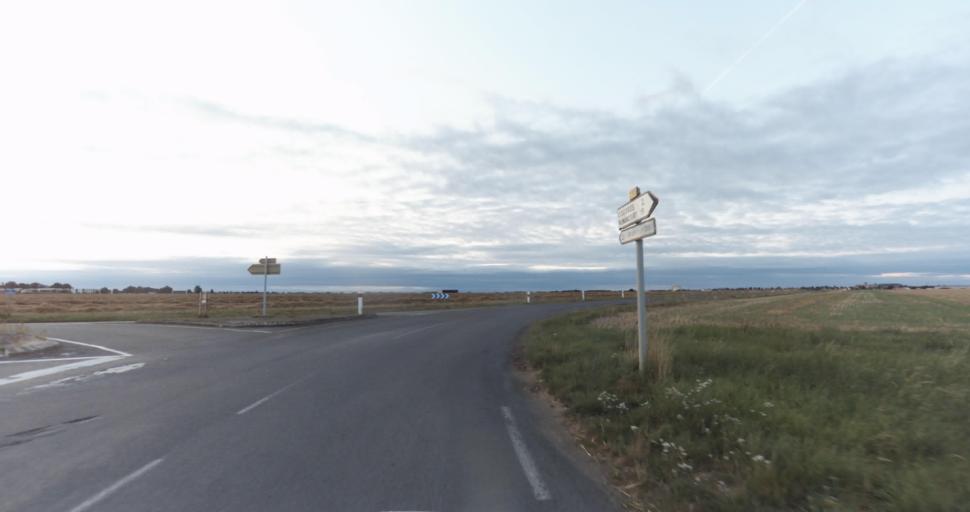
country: FR
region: Haute-Normandie
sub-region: Departement de l'Eure
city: Marcilly-sur-Eure
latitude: 48.8851
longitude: 1.2626
